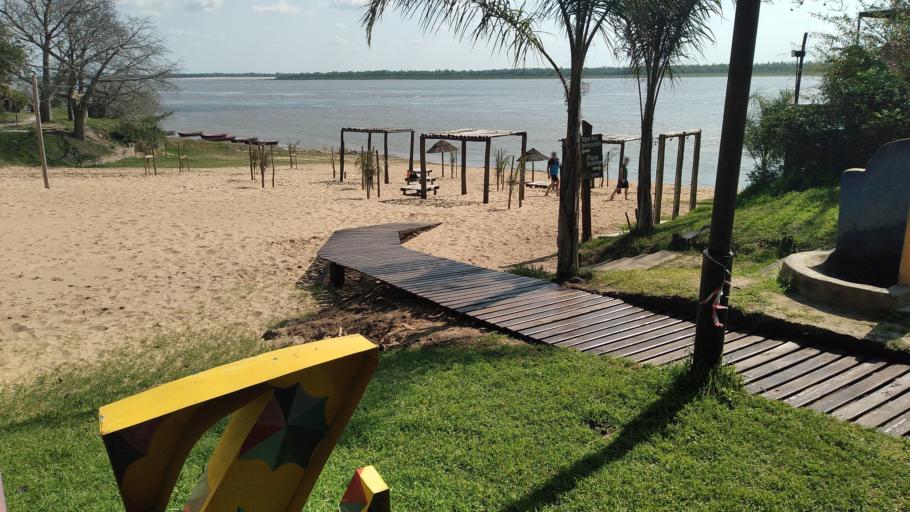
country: AR
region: Entre Rios
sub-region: Departamento de La Paz
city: La Paz
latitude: -30.7383
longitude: -59.6472
